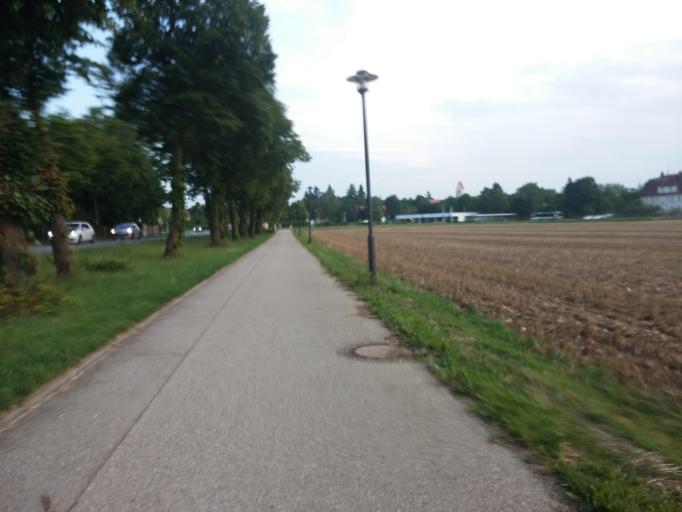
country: DE
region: Bavaria
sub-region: Upper Bavaria
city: Haar
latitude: 48.1181
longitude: 11.7428
